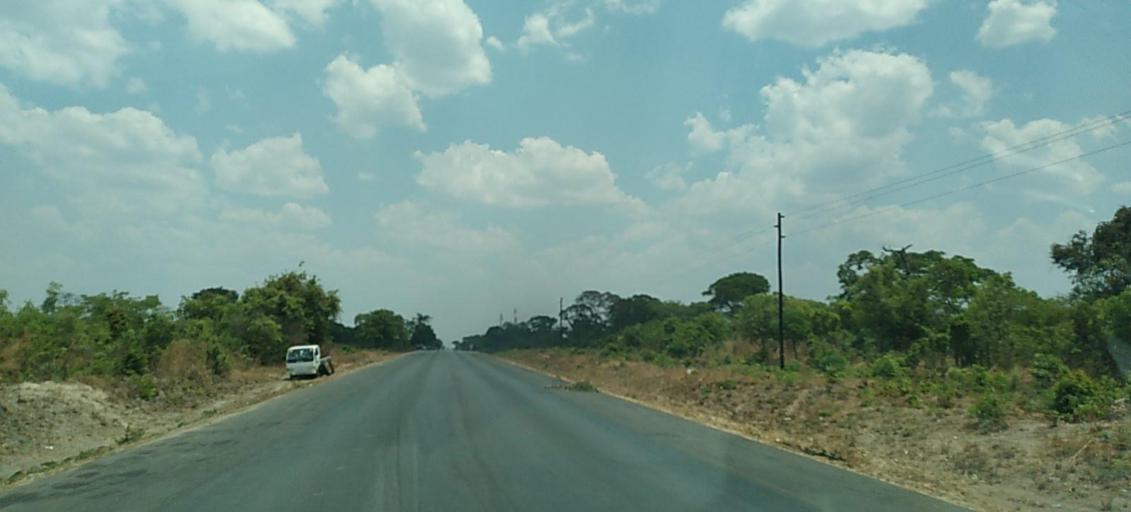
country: ZM
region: Central
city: Kapiri Mposhi
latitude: -14.1170
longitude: 28.6139
